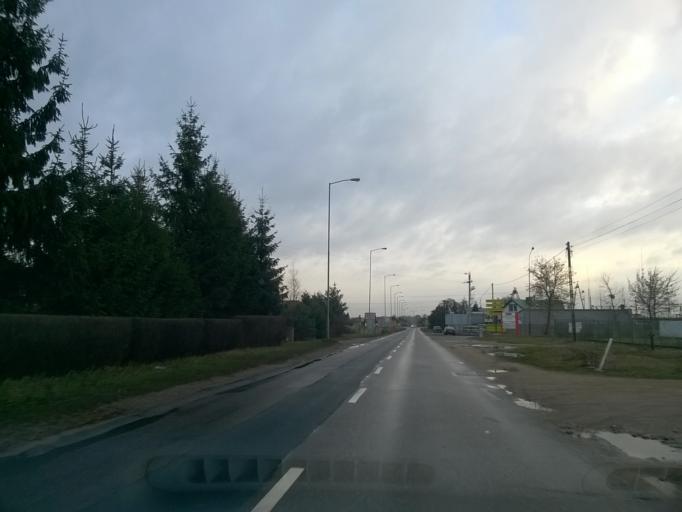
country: PL
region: Greater Poland Voivodeship
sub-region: Powiat wagrowiecki
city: Wagrowiec
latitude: 52.8202
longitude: 17.2256
